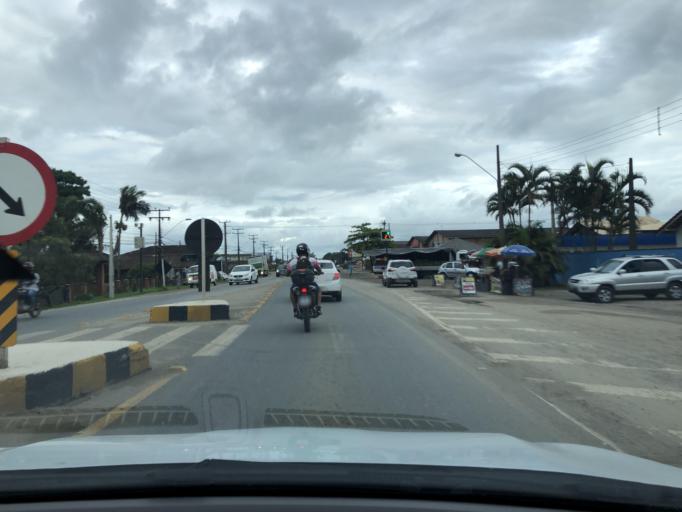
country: BR
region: Santa Catarina
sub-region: Joinville
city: Joinville
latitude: -26.4090
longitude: -48.7508
